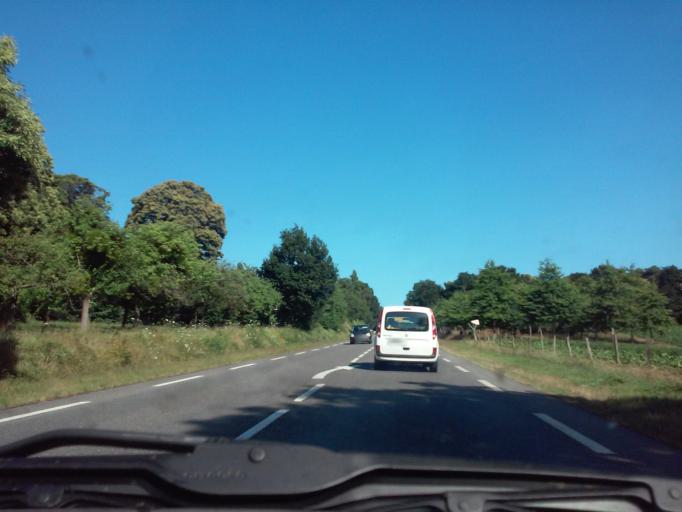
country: FR
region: Brittany
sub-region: Departement d'Ille-et-Vilaine
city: La Chapelle-Janson
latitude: 48.3152
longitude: -1.0620
